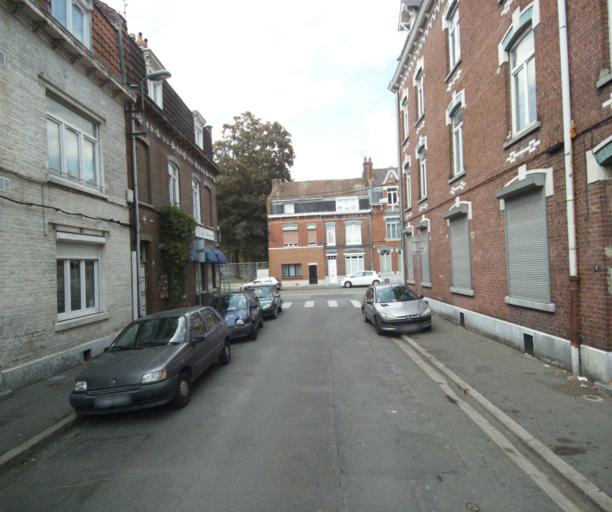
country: FR
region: Nord-Pas-de-Calais
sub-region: Departement du Nord
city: Mons-en-Baroeul
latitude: 50.6339
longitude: 3.0965
